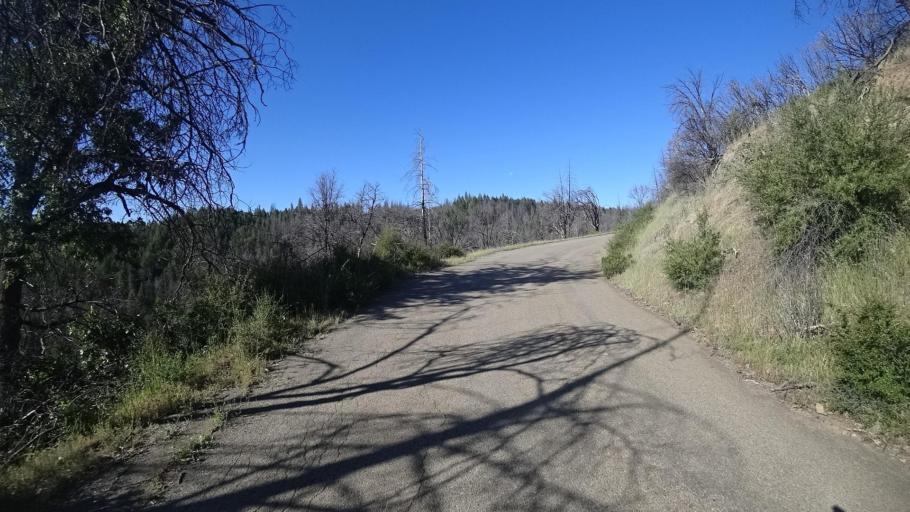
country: US
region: California
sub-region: Lake County
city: Upper Lake
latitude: 39.3965
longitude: -122.9613
